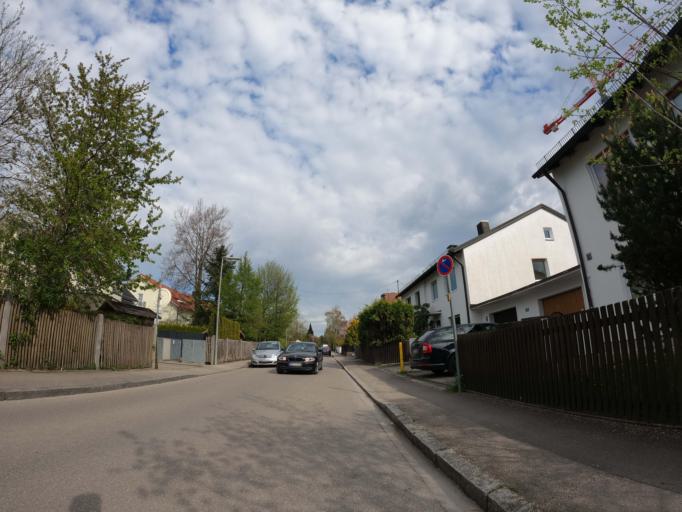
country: DE
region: Bavaria
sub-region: Upper Bavaria
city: Neubiberg
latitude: 48.1037
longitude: 11.6624
